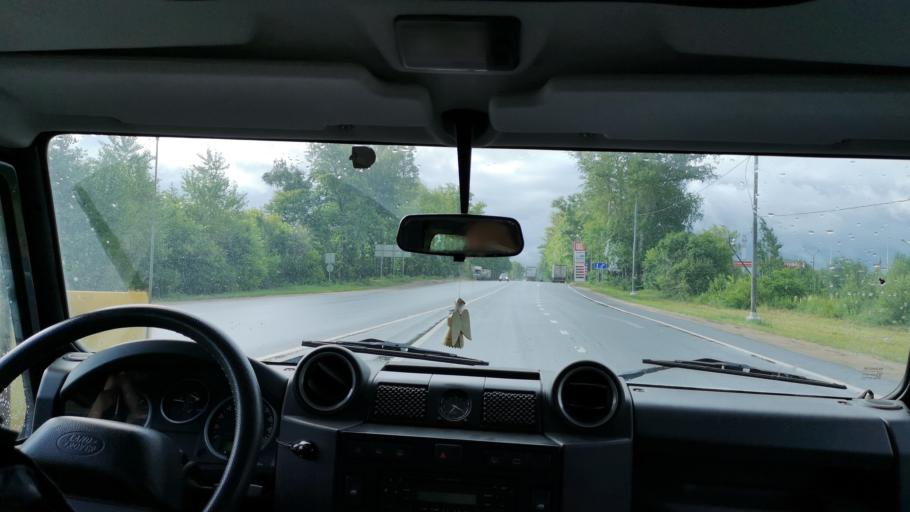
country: RU
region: Moskovskaya
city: Dmitrov
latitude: 56.3630
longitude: 37.4800
